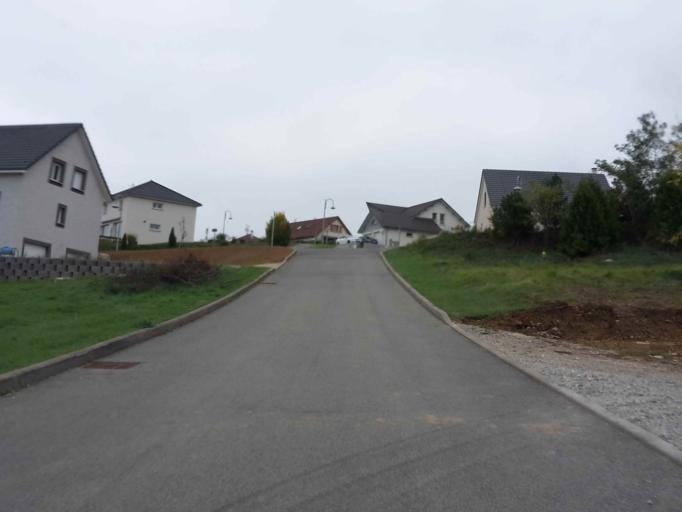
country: FR
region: Franche-Comte
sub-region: Departement du Doubs
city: Baume-les-Dames
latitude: 47.3527
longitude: 6.3379
